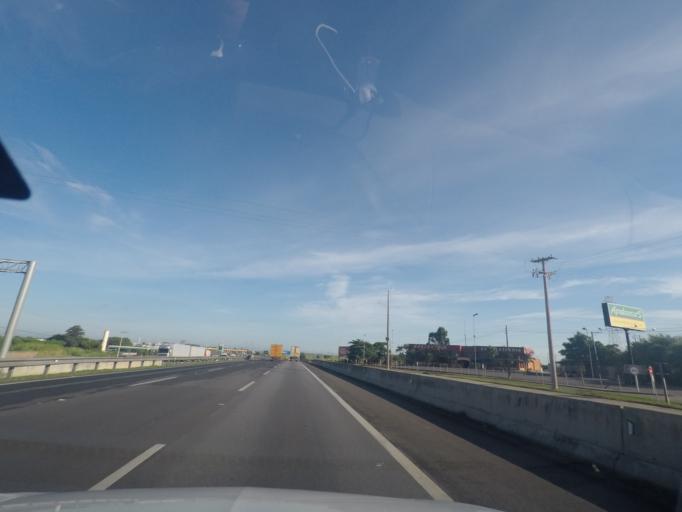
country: BR
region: Sao Paulo
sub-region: Sumare
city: Sumare
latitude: -22.7776
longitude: -47.2335
